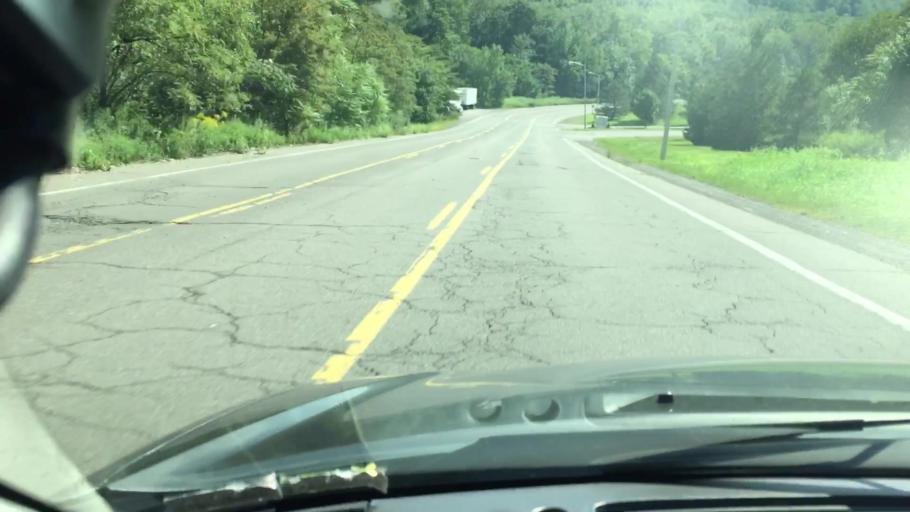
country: US
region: Pennsylvania
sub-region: Luzerne County
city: Plymouth
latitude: 41.1977
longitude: -75.9424
